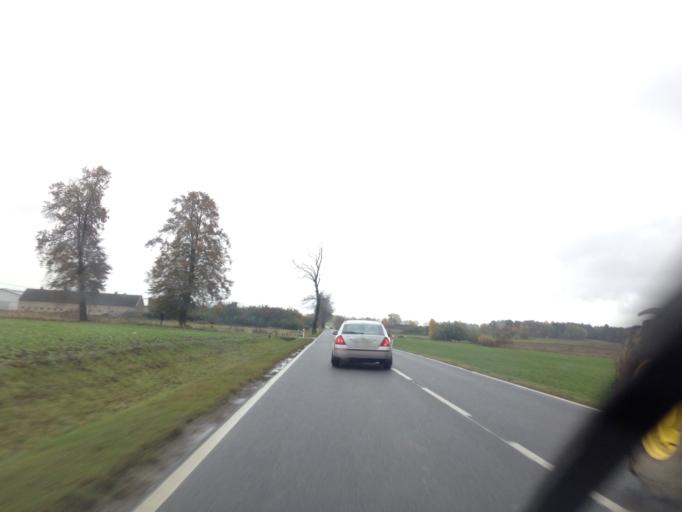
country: PL
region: Warmian-Masurian Voivodeship
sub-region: Powiat nowomiejski
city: Biskupiec
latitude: 53.6003
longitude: 19.4133
